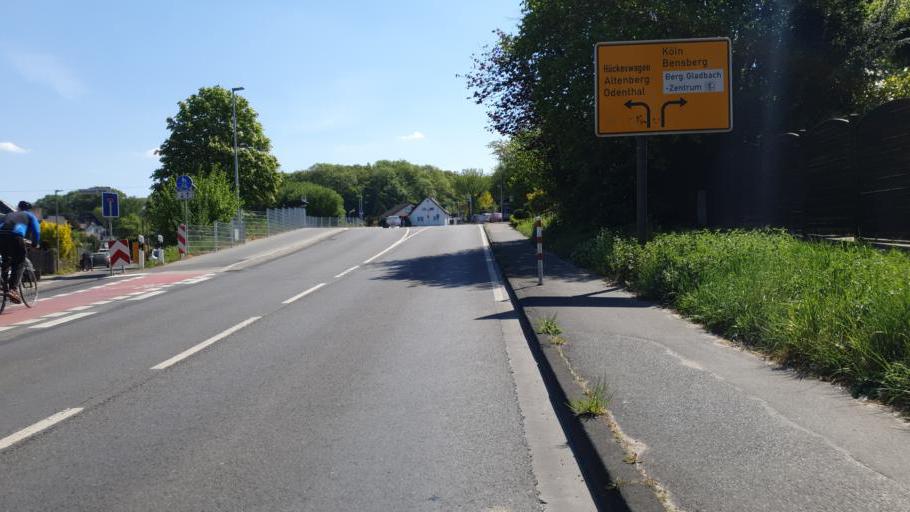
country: DE
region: North Rhine-Westphalia
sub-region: Regierungsbezirk Koln
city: Odenthal
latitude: 51.0227
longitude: 7.0837
